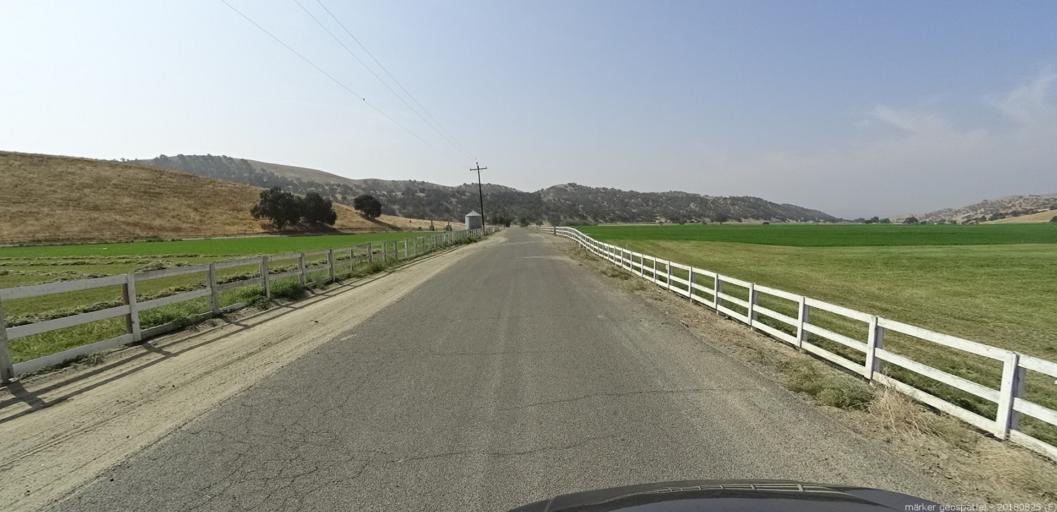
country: US
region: California
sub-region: San Luis Obispo County
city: San Miguel
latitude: 35.8285
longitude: -120.6554
